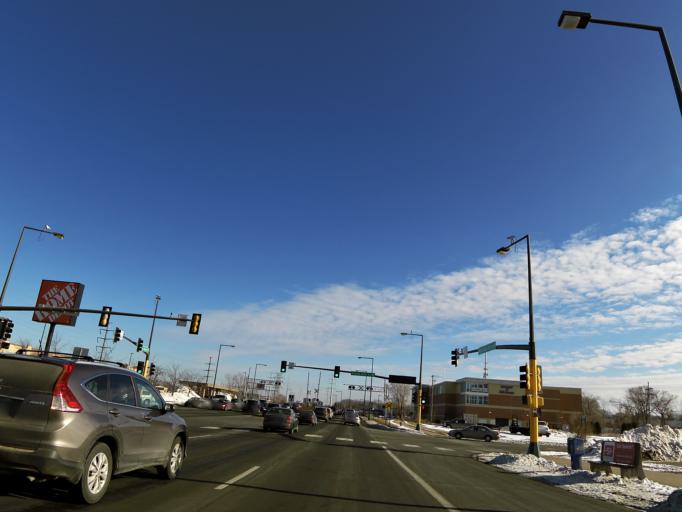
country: US
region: Minnesota
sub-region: Hennepin County
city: Bloomington
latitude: 44.8593
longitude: -93.2849
